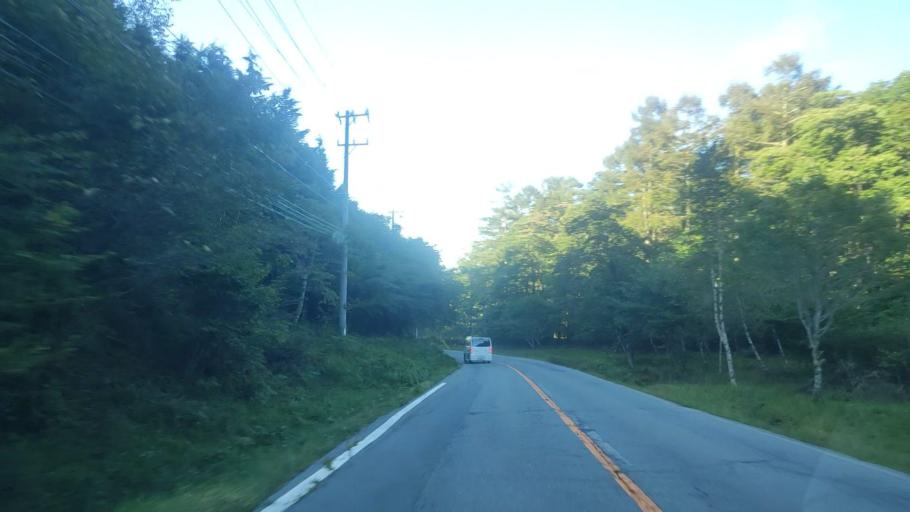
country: JP
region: Nagano
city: Kamimaruko
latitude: 36.1910
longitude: 138.2871
